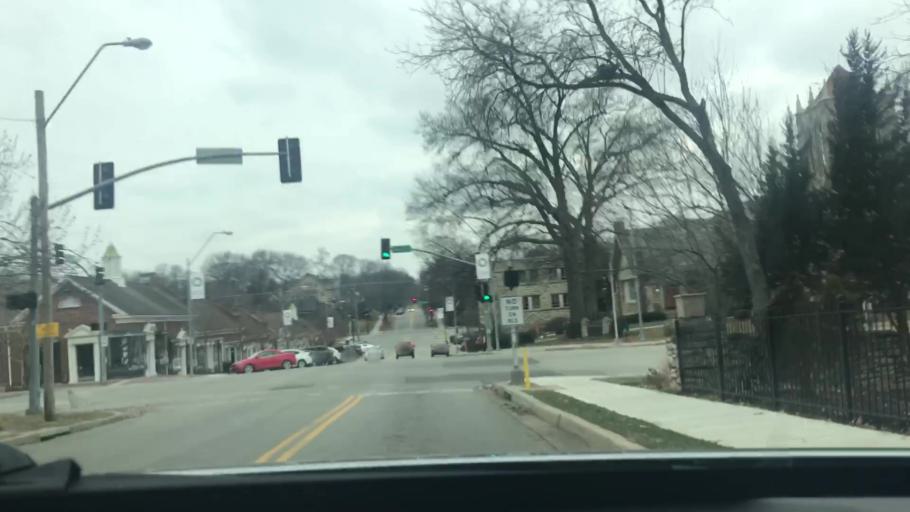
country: US
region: Kansas
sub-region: Johnson County
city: Mission Hills
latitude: 39.0275
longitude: -94.5827
